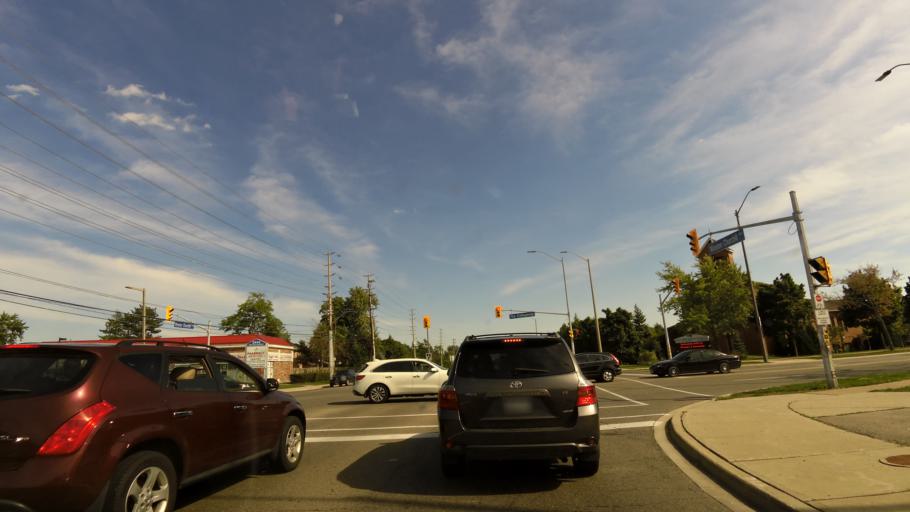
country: CA
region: Ontario
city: Mississauga
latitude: 43.5310
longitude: -79.6929
